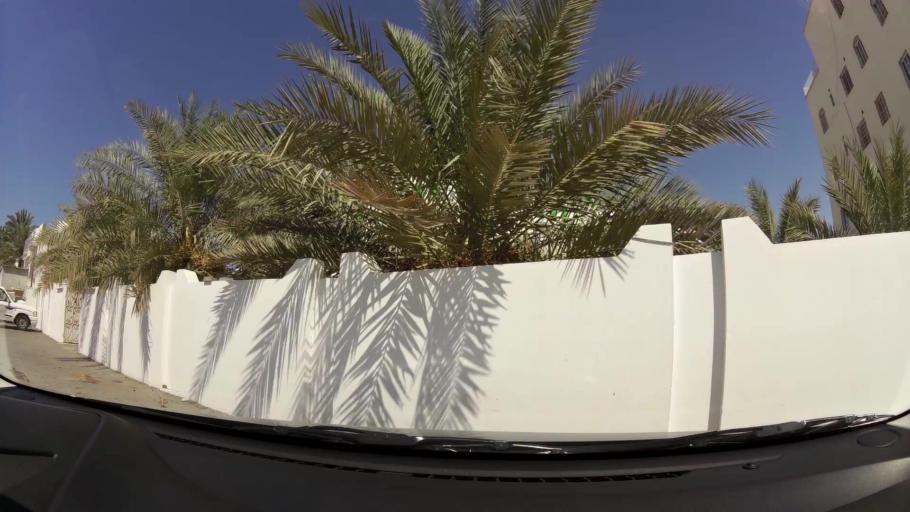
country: OM
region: Muhafazat Masqat
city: As Sib al Jadidah
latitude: 23.6284
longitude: 58.2206
